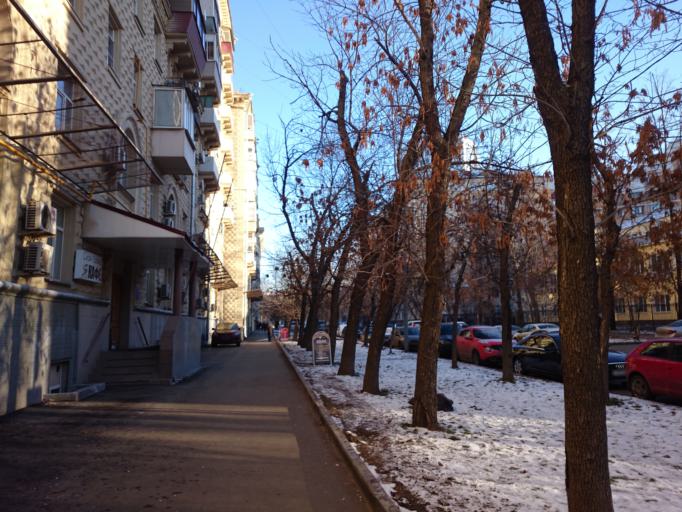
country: RU
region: Moscow
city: Sokol
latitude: 55.7997
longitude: 37.5263
